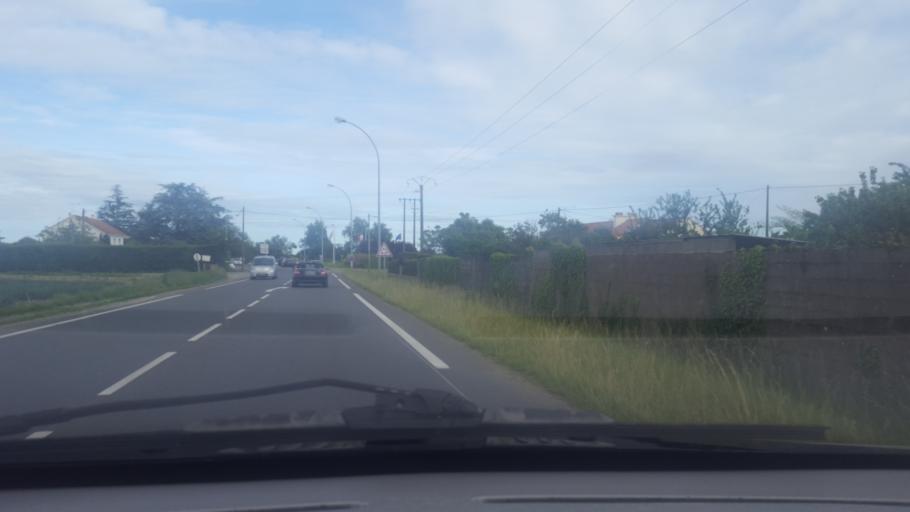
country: FR
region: Pays de la Loire
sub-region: Departement de la Loire-Atlantique
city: Machecoul
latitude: 46.9909
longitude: -1.7985
